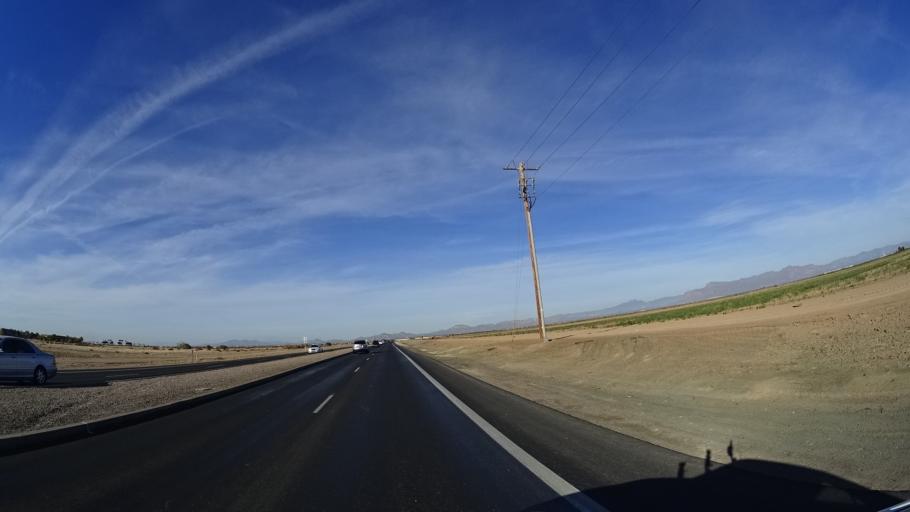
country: US
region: Arizona
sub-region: Maricopa County
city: Queen Creek
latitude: 33.2796
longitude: -111.6347
